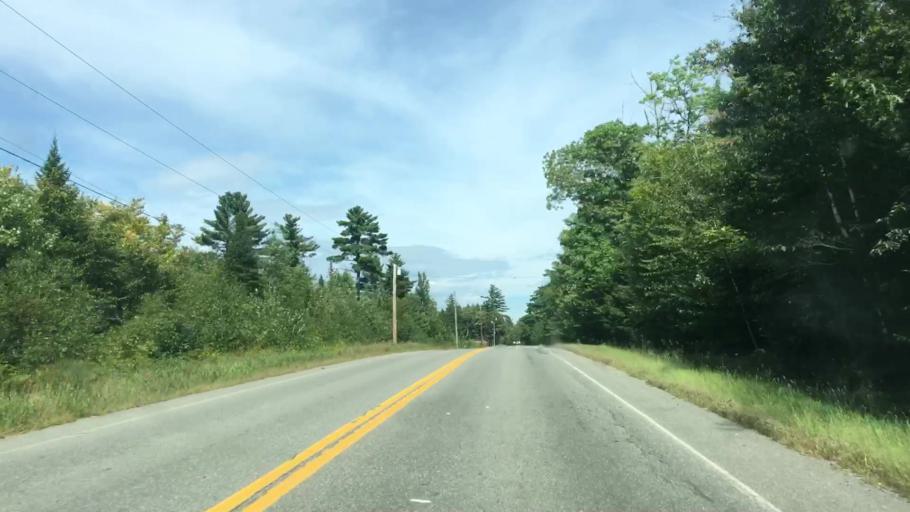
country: US
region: Maine
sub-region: Penobscot County
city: Lincoln
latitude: 45.3727
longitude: -68.5553
